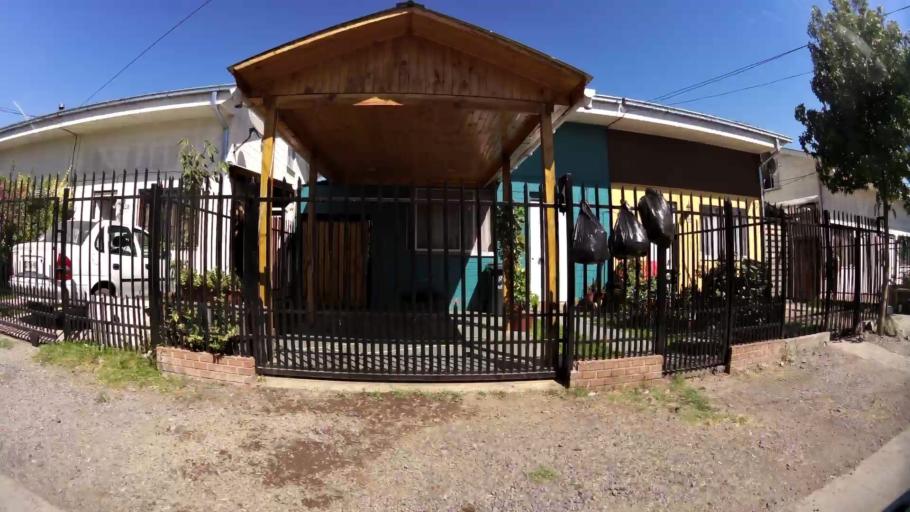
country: CL
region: Maule
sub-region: Provincia de Curico
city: Curico
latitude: -34.9660
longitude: -71.2466
